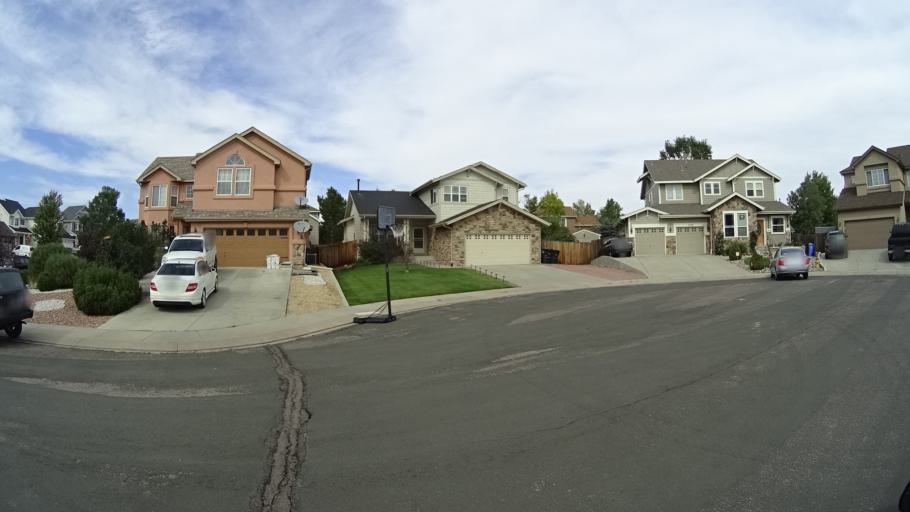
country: US
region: Colorado
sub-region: El Paso County
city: Cimarron Hills
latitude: 38.9078
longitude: -104.6984
